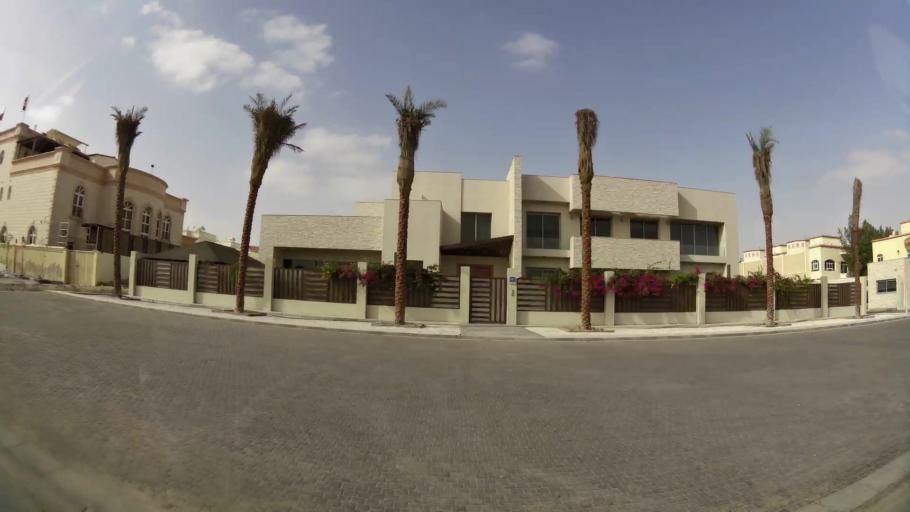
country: AE
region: Abu Dhabi
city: Abu Dhabi
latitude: 24.4045
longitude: 54.5925
